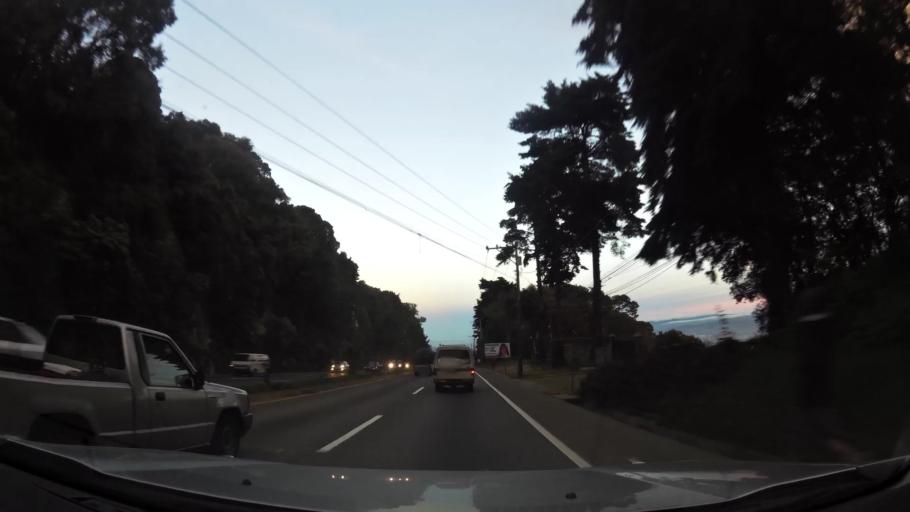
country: GT
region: Sacatepequez
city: San Lucas Sacatepequez
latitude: 14.6001
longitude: -90.6361
